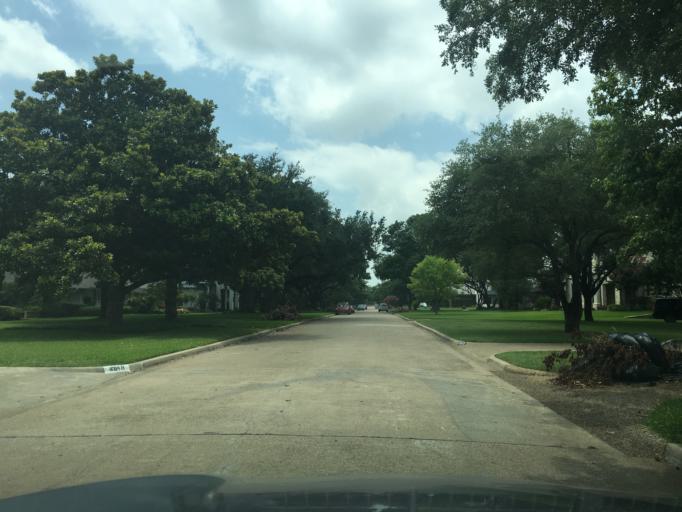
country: US
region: Texas
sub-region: Dallas County
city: University Park
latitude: 32.8963
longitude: -96.8252
